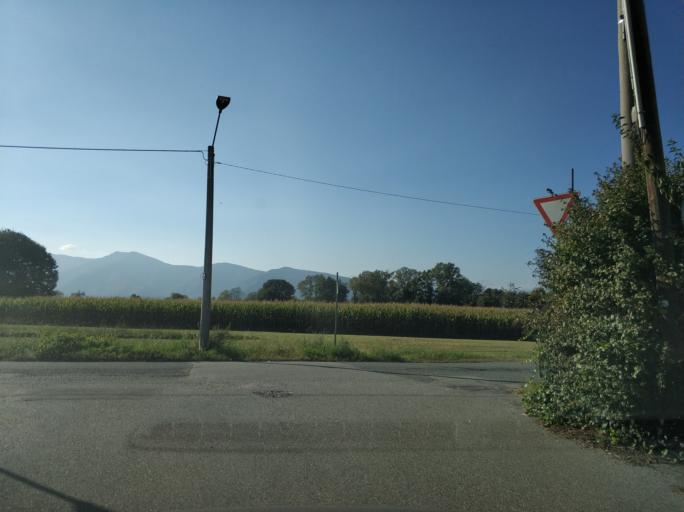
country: IT
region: Piedmont
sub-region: Provincia di Torino
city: Cirie
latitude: 45.2282
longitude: 7.5929
